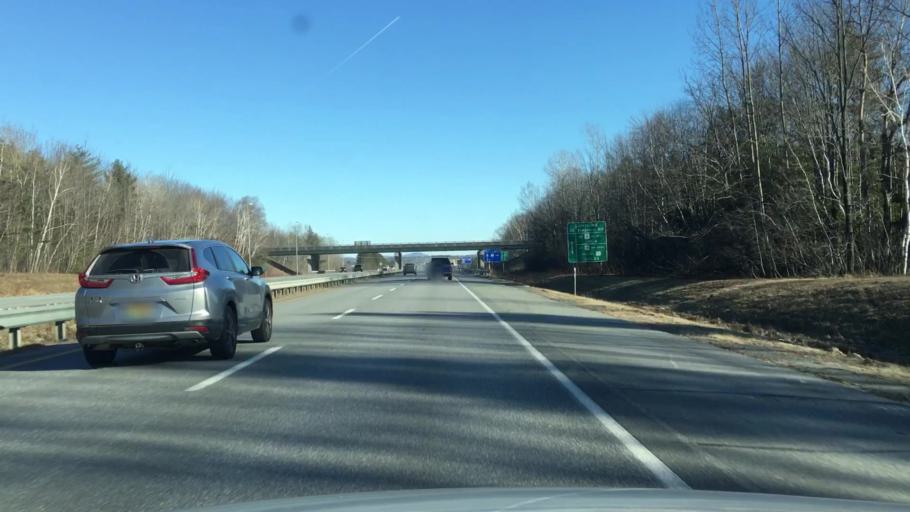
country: US
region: Maine
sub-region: Penobscot County
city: Bangor
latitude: 44.7863
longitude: -68.7969
